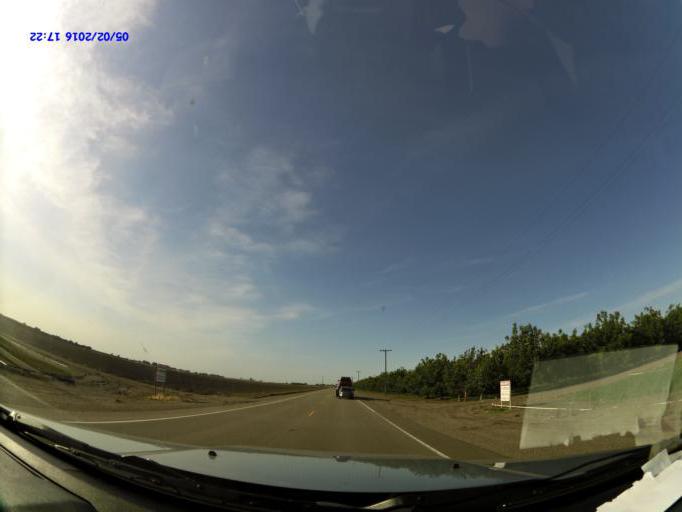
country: US
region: California
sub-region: San Joaquin County
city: Manteca
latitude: 37.8554
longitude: -121.1456
